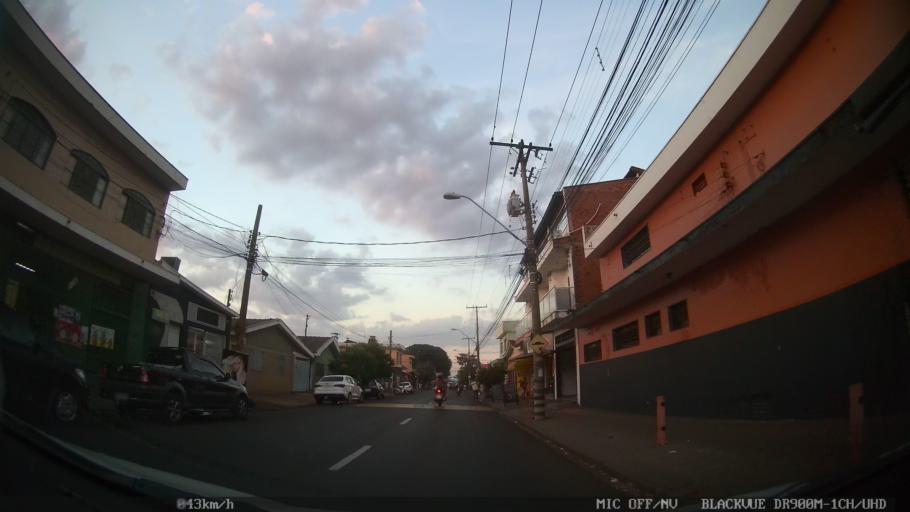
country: BR
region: Sao Paulo
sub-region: Ribeirao Preto
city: Ribeirao Preto
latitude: -21.1481
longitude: -47.8215
